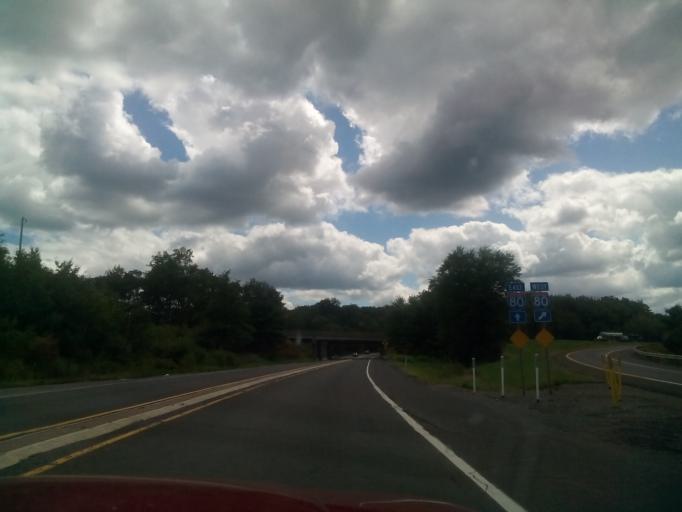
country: US
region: Pennsylvania
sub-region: Luzerne County
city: White Haven
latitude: 41.0680
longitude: -75.7019
